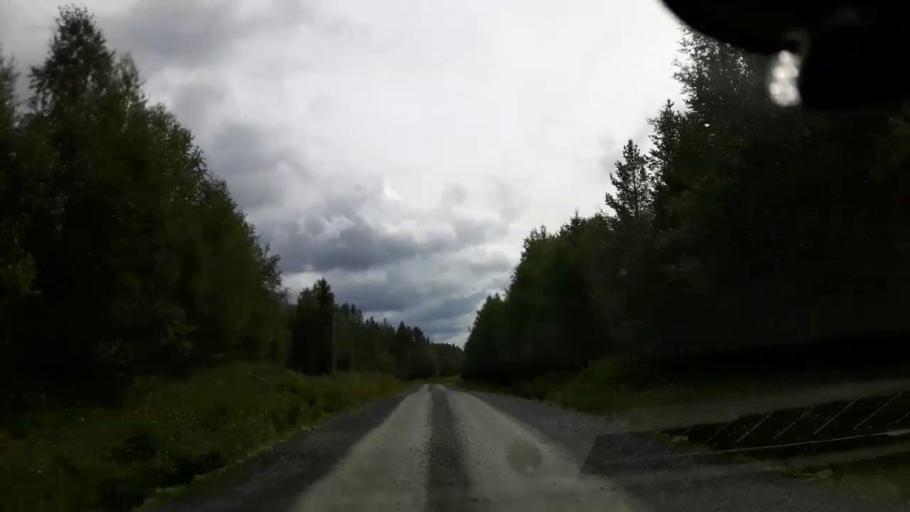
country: SE
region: Jaemtland
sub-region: Krokoms Kommun
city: Valla
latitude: 63.5954
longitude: 14.1392
